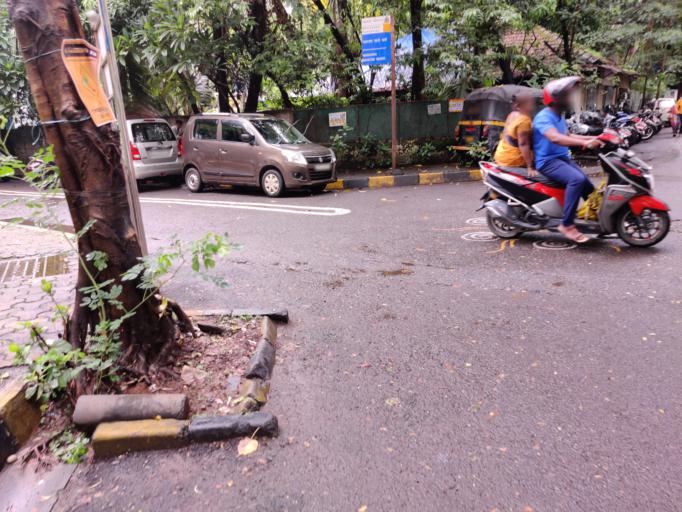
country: IN
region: Maharashtra
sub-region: Mumbai Suburban
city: Borivli
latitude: 19.2511
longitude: 72.8574
